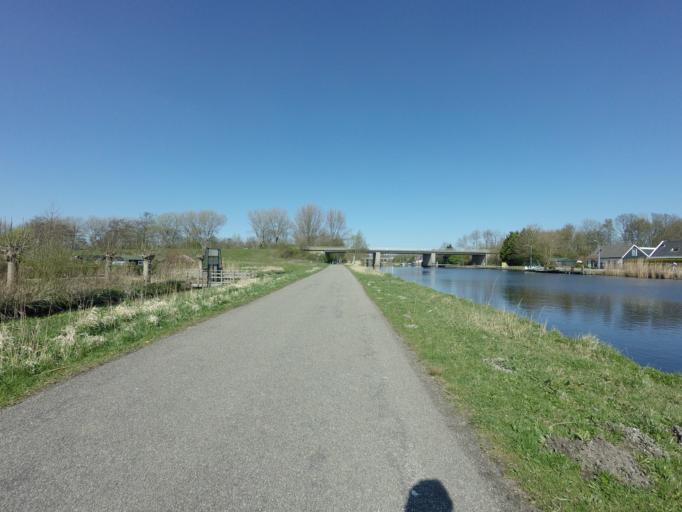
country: NL
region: North Holland
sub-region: Gemeente Haarlem
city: Haarlem
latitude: 52.3671
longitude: 4.6725
